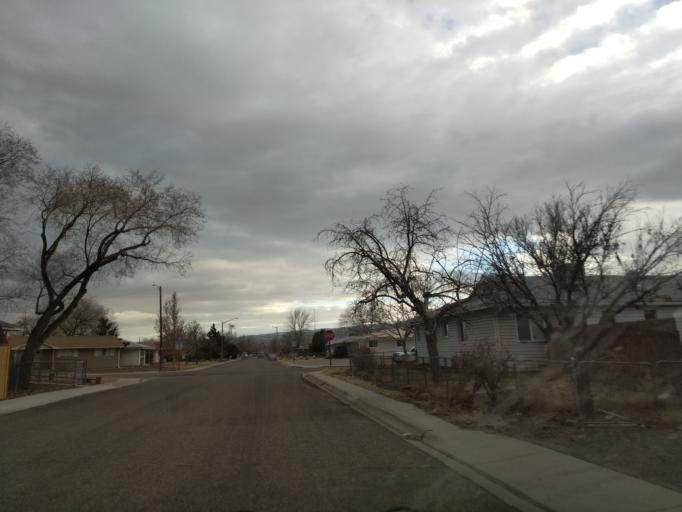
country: US
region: Colorado
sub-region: Mesa County
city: Grand Junction
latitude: 39.0738
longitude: -108.5352
